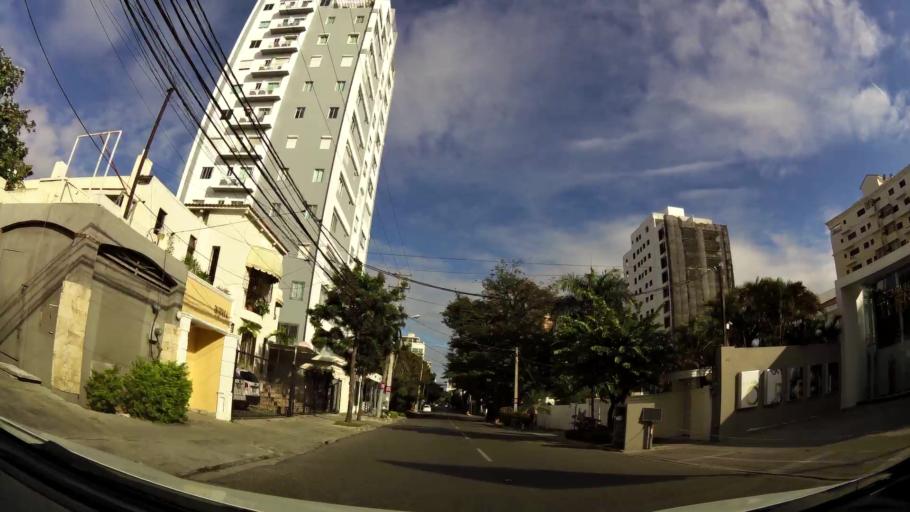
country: DO
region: Nacional
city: La Julia
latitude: 18.4703
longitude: -69.9355
